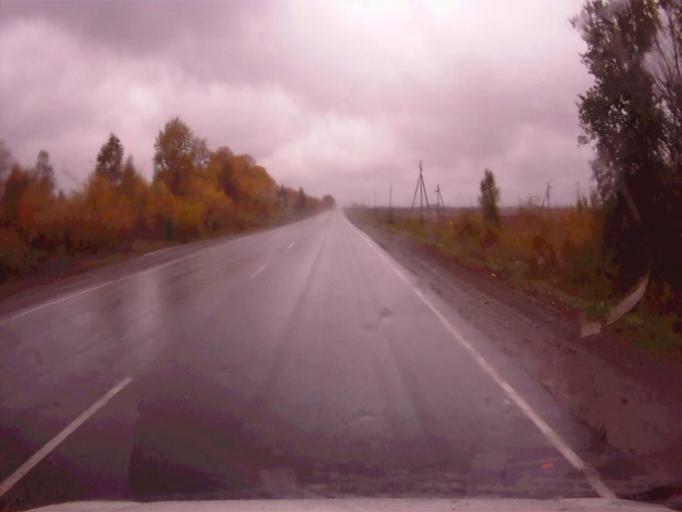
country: RU
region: Chelyabinsk
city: Argayash
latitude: 55.4247
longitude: 61.0057
